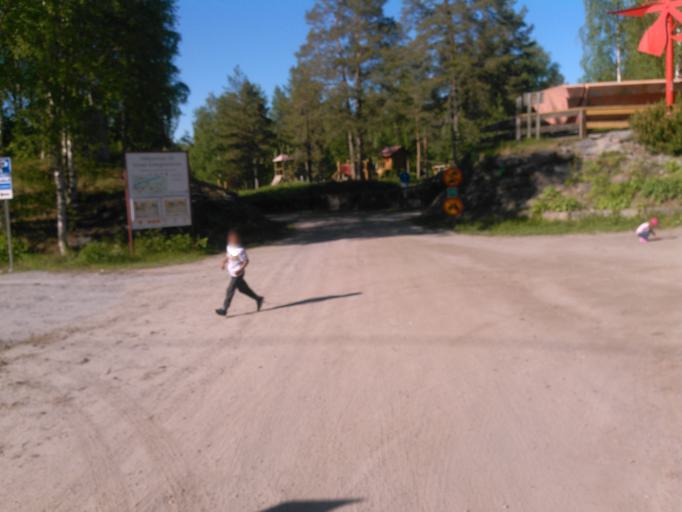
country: SE
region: Vaesterbotten
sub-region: Umea Kommun
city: Roback
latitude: 63.8343
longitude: 20.1190
